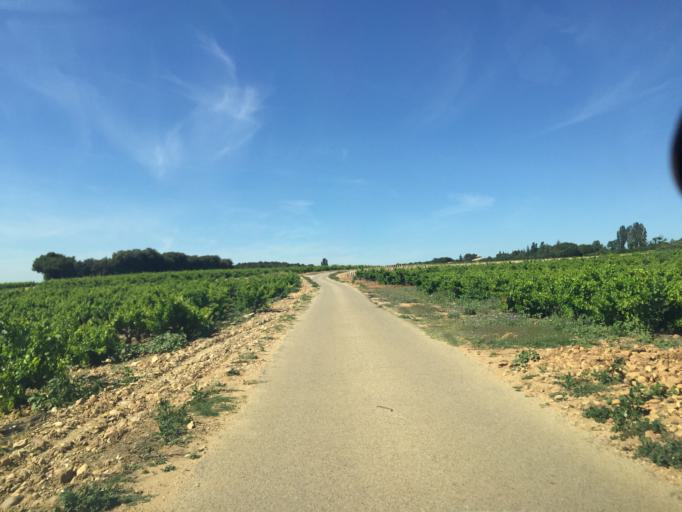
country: FR
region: Provence-Alpes-Cote d'Azur
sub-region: Departement du Vaucluse
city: Chateauneuf-du-Pape
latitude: 44.0748
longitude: 4.8066
